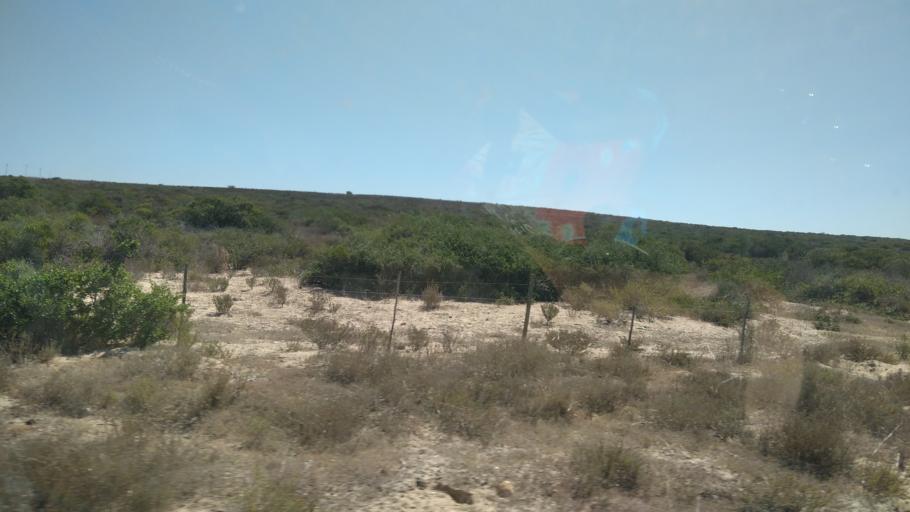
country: ZA
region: Western Cape
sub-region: West Coast District Municipality
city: Vredenburg
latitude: -33.0086
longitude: 18.1198
